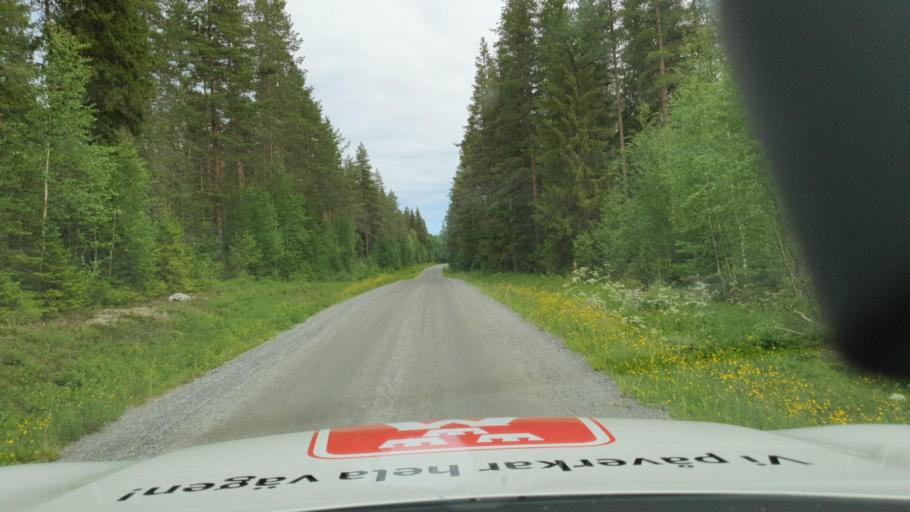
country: SE
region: Vaesterbotten
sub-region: Skelleftea Kommun
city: Forsbacka
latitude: 64.5237
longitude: 20.3268
